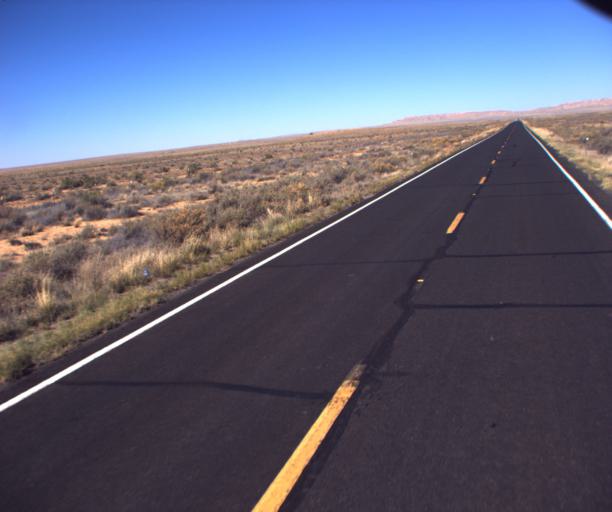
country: US
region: Arizona
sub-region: Navajo County
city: First Mesa
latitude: 35.6897
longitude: -110.5036
